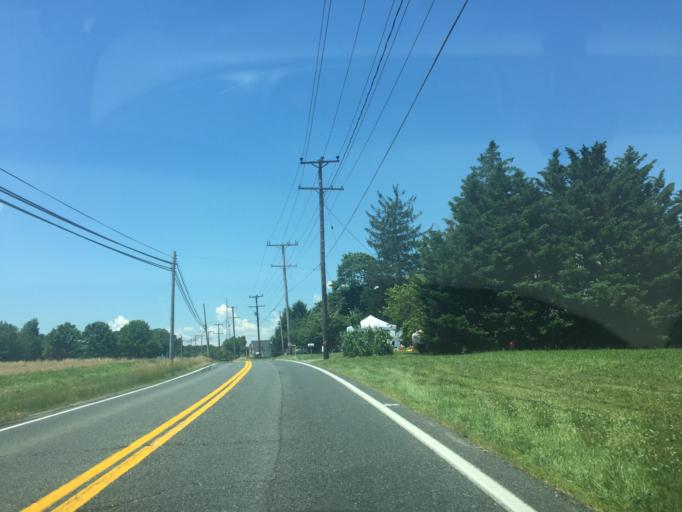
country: US
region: Maryland
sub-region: Harford County
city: Jarrettsville
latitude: 39.6119
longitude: -76.5026
